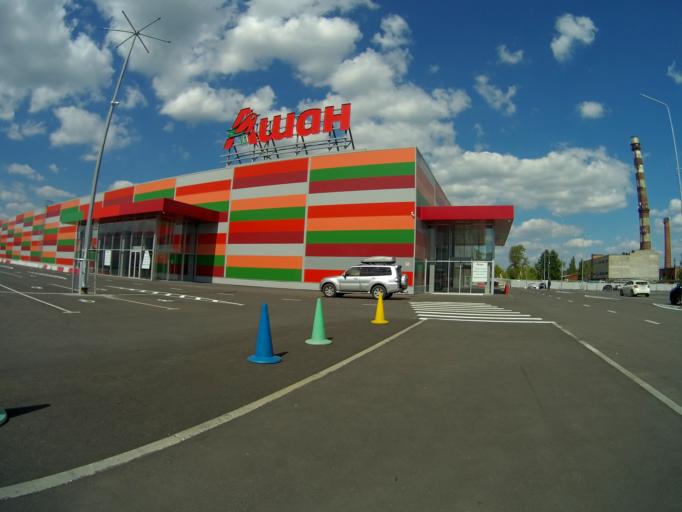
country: RU
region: Vladimir
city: Vladimir
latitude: 56.1495
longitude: 40.3892
